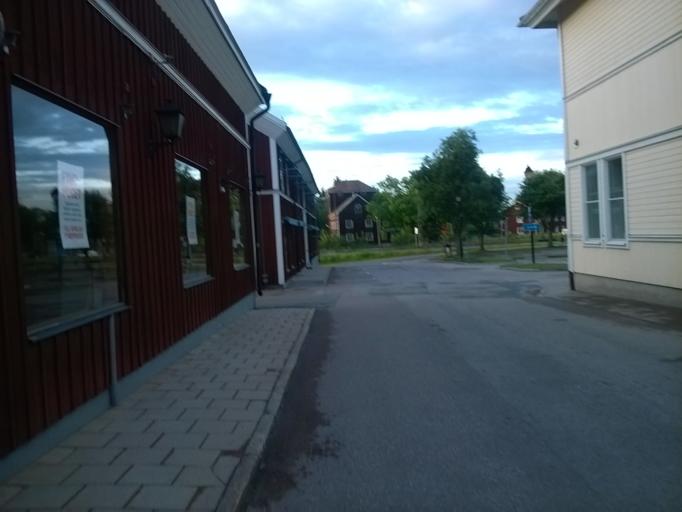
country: SE
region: Dalarna
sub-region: Saters Kommun
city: Saeter
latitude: 60.3476
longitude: 15.7489
